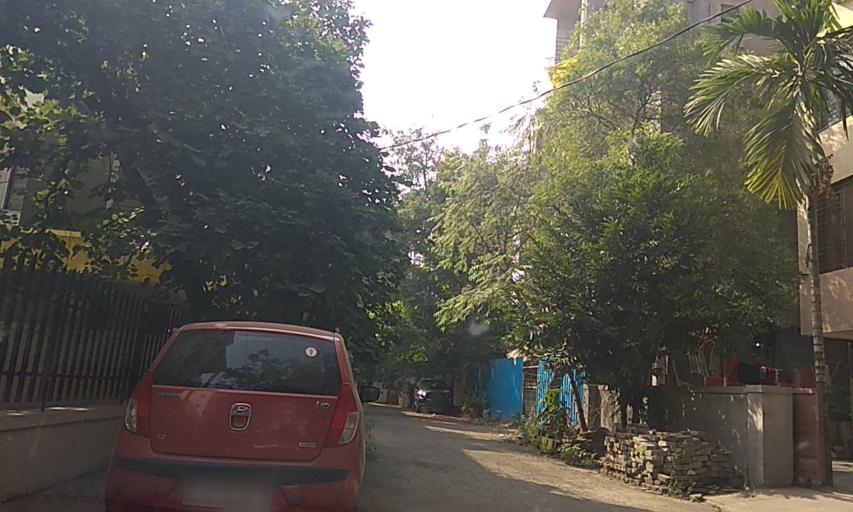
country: IN
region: Maharashtra
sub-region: Pune Division
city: Pimpri
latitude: 18.5622
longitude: 73.7771
